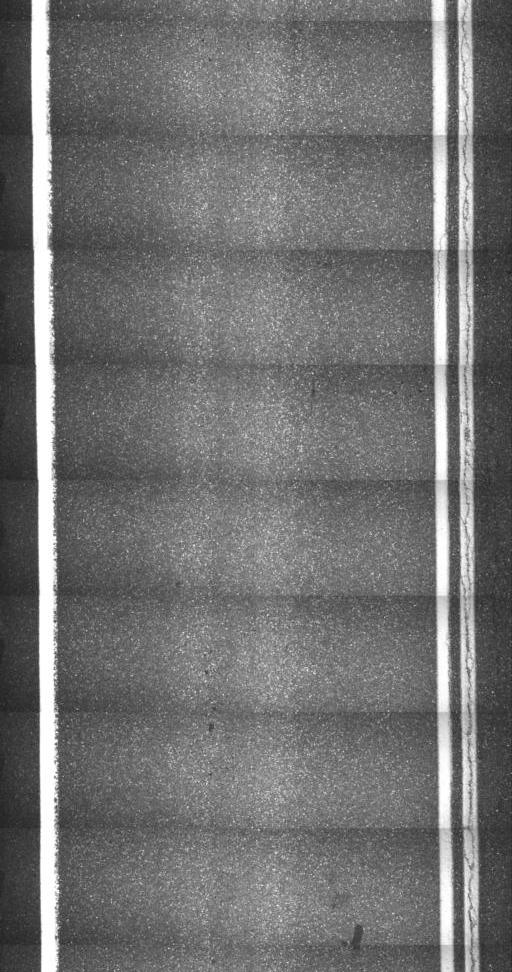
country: US
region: Vermont
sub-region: Windham County
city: Dover
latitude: 42.8004
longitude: -72.8248
